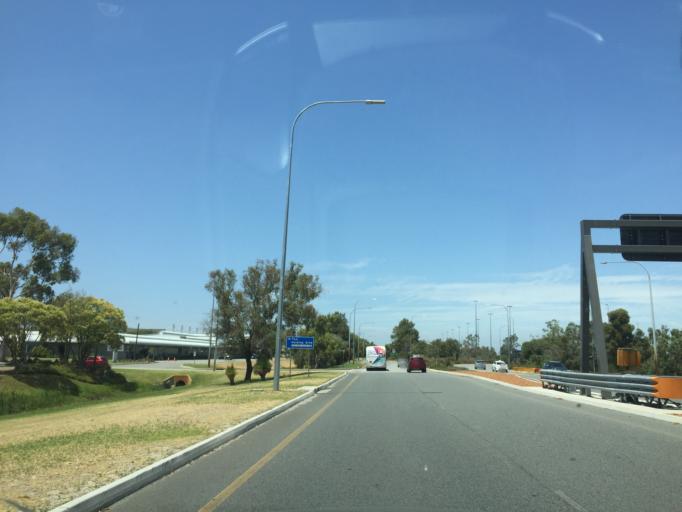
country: AU
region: Western Australia
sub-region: Belmont
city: Redcliffe
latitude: -31.9466
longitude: 115.9742
